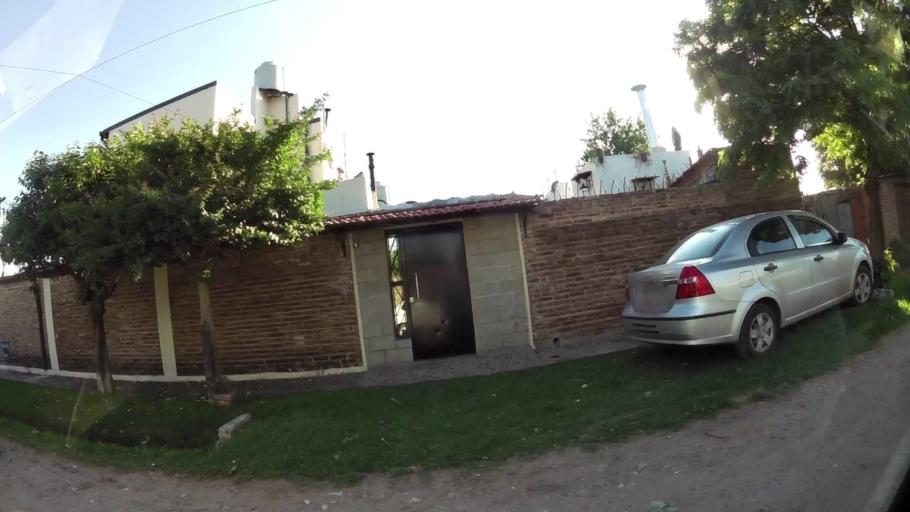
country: AR
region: Buenos Aires
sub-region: Partido de Merlo
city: Merlo
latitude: -34.6841
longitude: -58.7345
